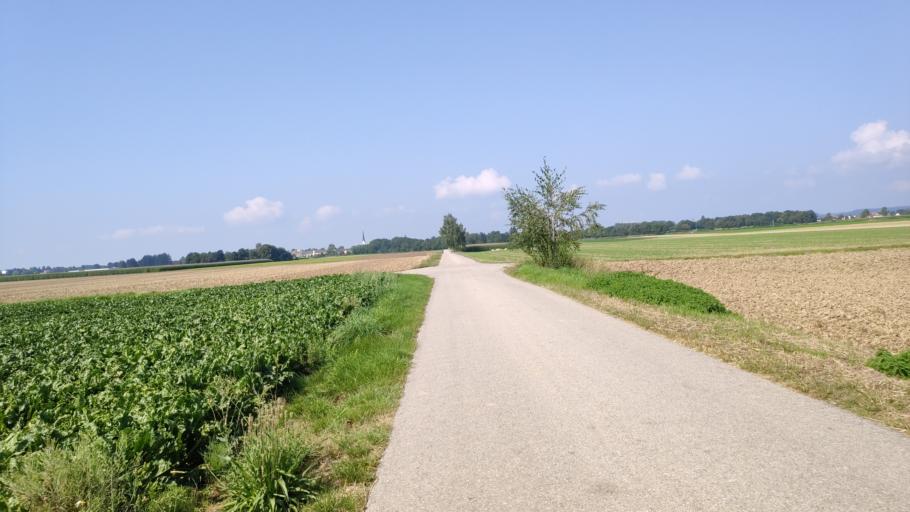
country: DE
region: Bavaria
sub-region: Swabia
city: Schwabmunchen
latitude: 48.1837
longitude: 10.7839
